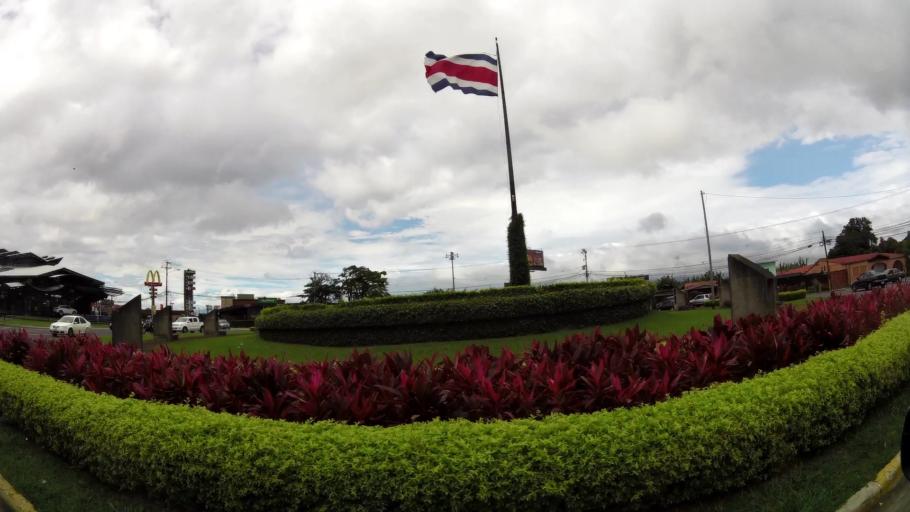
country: CR
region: San Jose
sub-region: Canton de Goicoechea
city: Guadalupe
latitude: 9.9392
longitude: -84.0546
